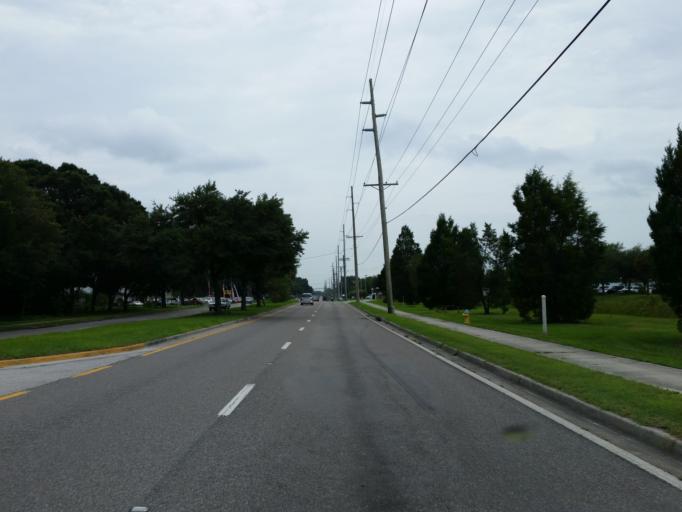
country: US
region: Florida
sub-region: Hillsborough County
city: Mango
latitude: 27.9608
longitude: -82.3353
